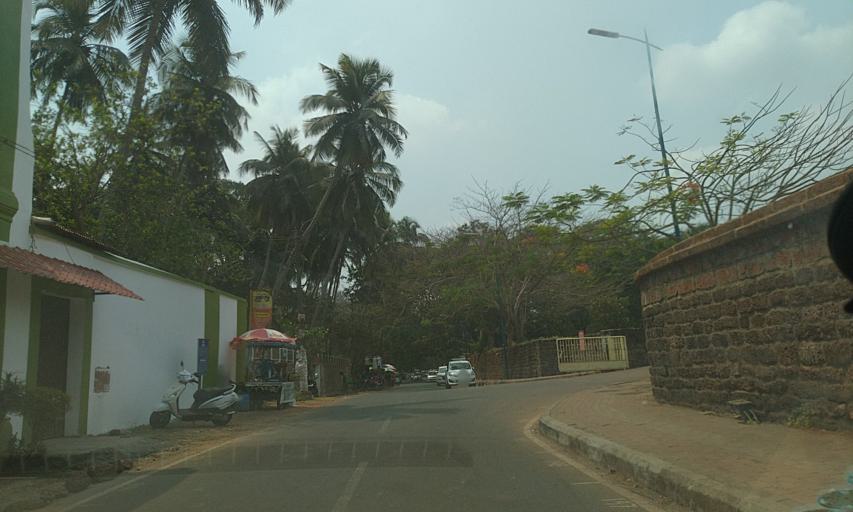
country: IN
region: Goa
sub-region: North Goa
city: Jua
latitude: 15.5043
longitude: 73.9137
